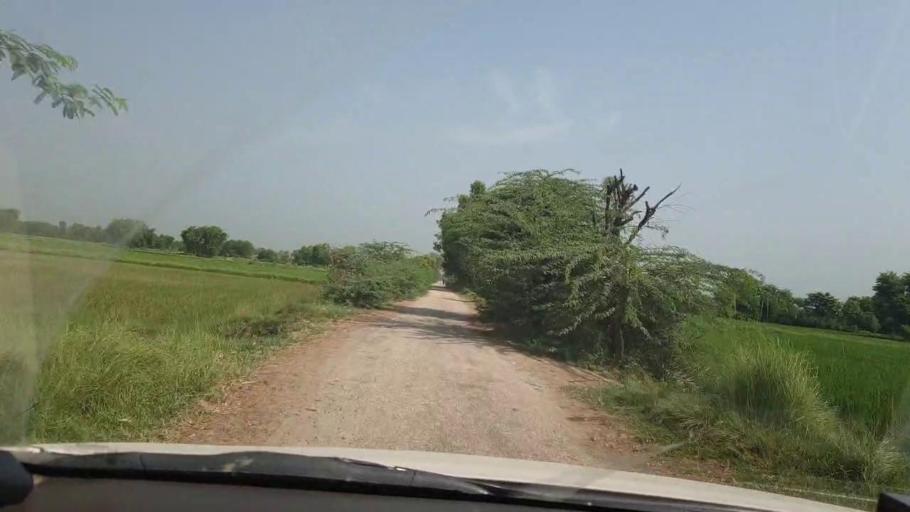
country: PK
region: Sindh
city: Chak
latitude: 27.8320
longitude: 68.7995
